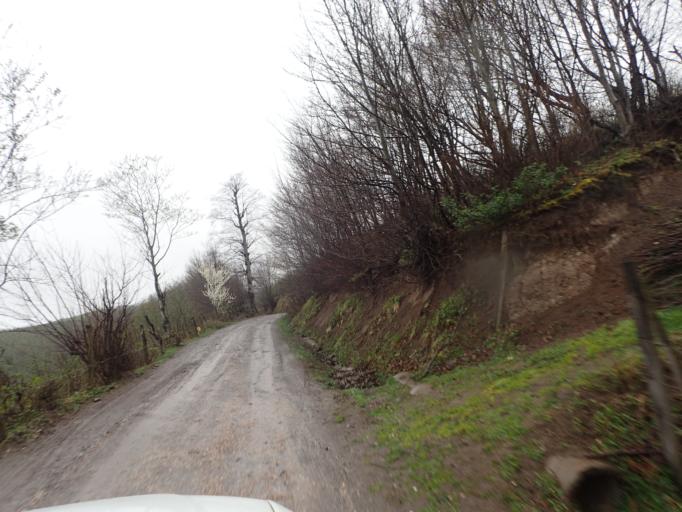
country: TR
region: Ordu
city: Korgan
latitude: 40.8058
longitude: 37.2842
